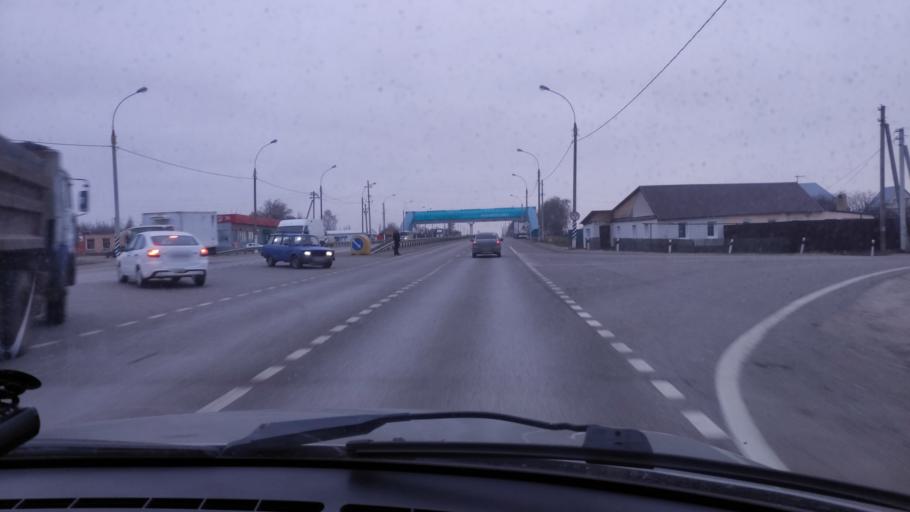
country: RU
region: Tambov
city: Komsomolets
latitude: 52.7292
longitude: 41.3241
